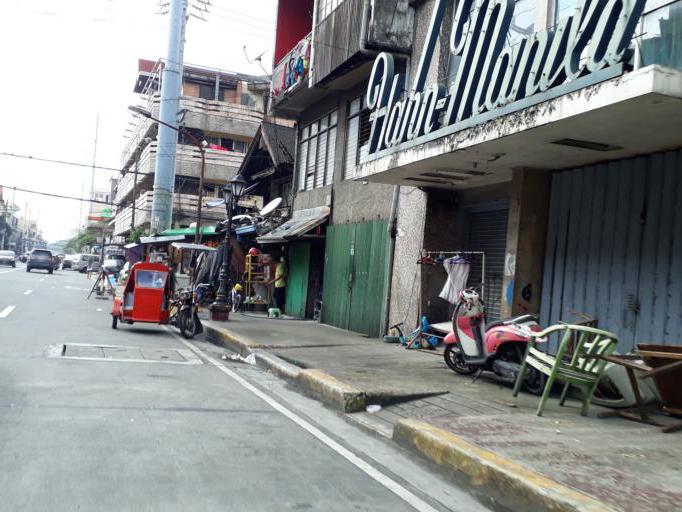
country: PH
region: Metro Manila
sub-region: City of Manila
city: Manila
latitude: 14.6205
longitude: 120.9921
